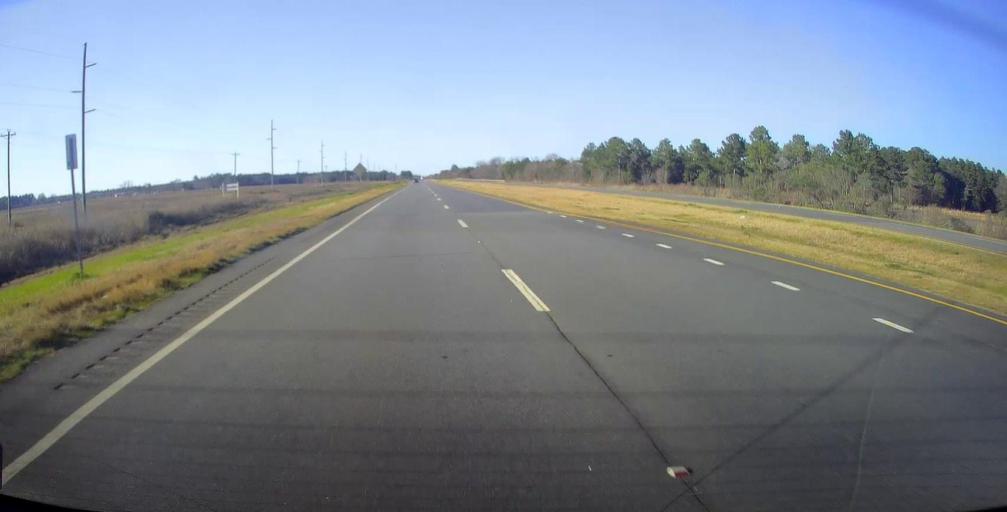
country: US
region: Georgia
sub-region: Lee County
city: Leesburg
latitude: 31.7910
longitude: -84.2002
